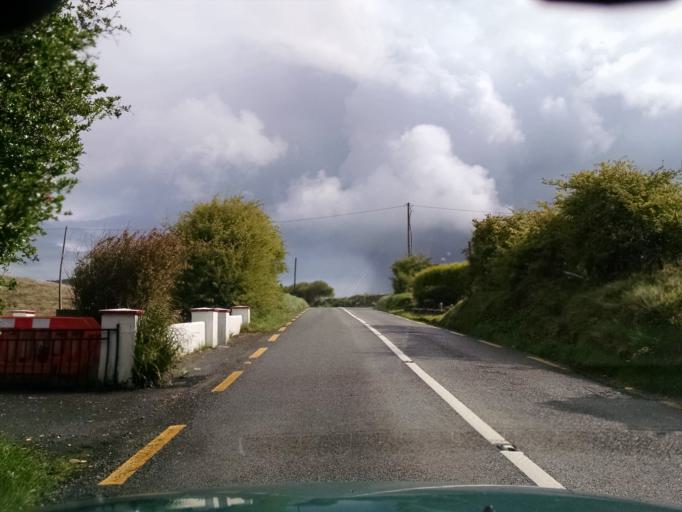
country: IE
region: Connaught
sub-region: County Galway
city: Bearna
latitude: 53.0361
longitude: -9.2872
